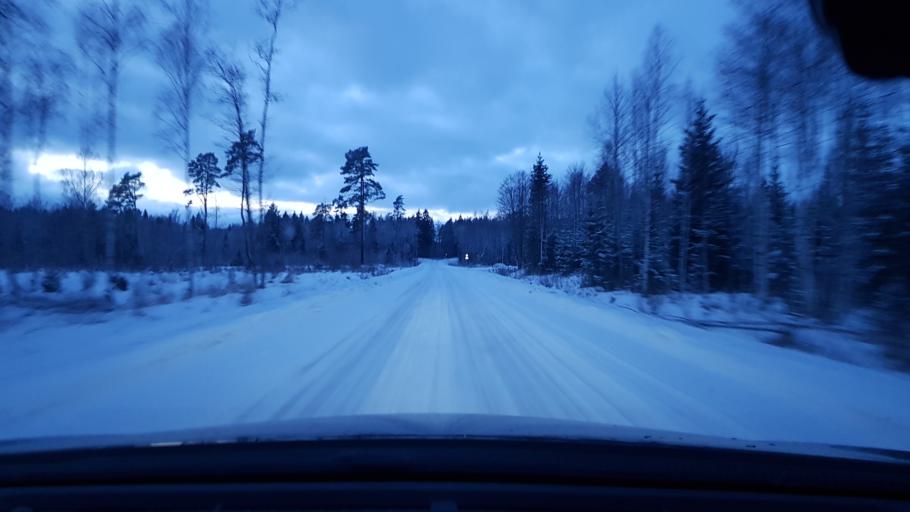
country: EE
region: Harju
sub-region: Nissi vald
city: Turba
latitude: 59.1286
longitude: 24.0774
